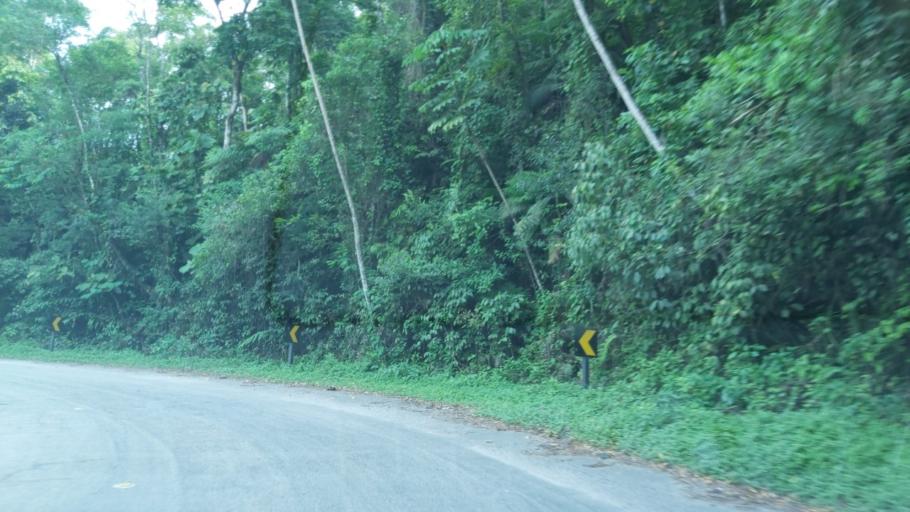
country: BR
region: Sao Paulo
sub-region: Miracatu
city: Miracatu
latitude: -24.0522
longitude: -47.5711
